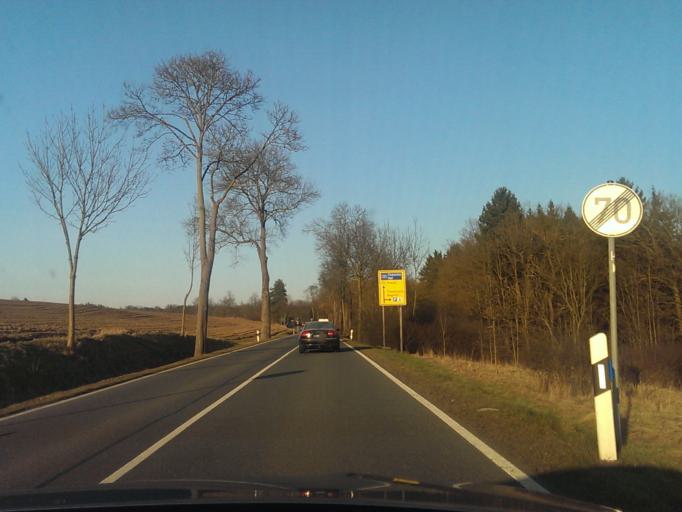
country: DE
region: Saxony
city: Weischlitz
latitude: 50.4280
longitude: 12.0848
